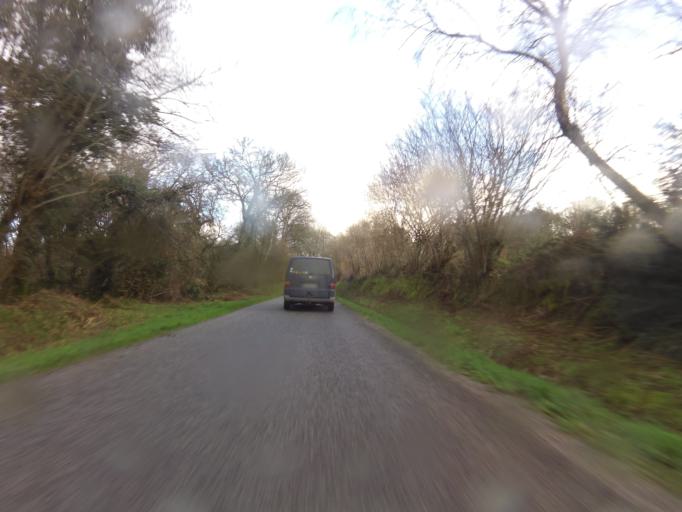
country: FR
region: Brittany
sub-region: Departement des Cotes-d'Armor
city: Rostrenen
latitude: 48.1713
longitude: -3.3156
